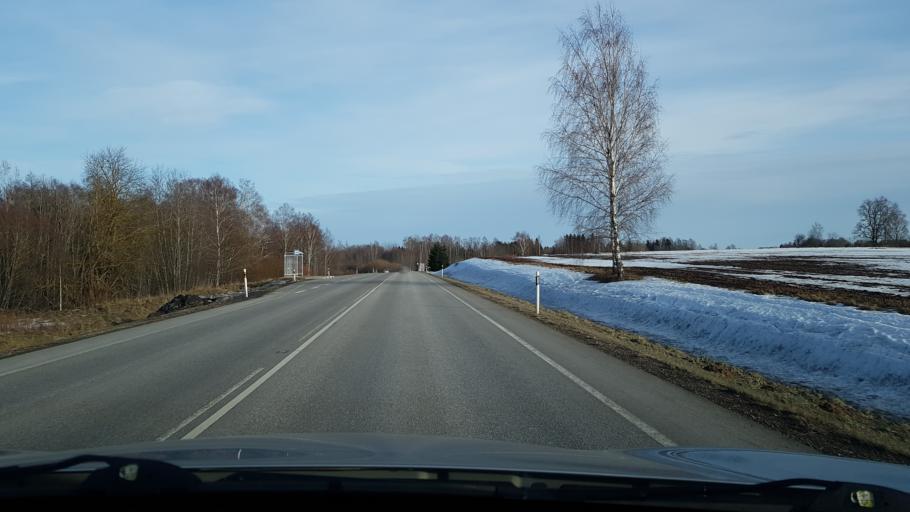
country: EE
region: Viljandimaa
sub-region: Viiratsi vald
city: Viiratsi
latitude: 58.3910
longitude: 25.7914
